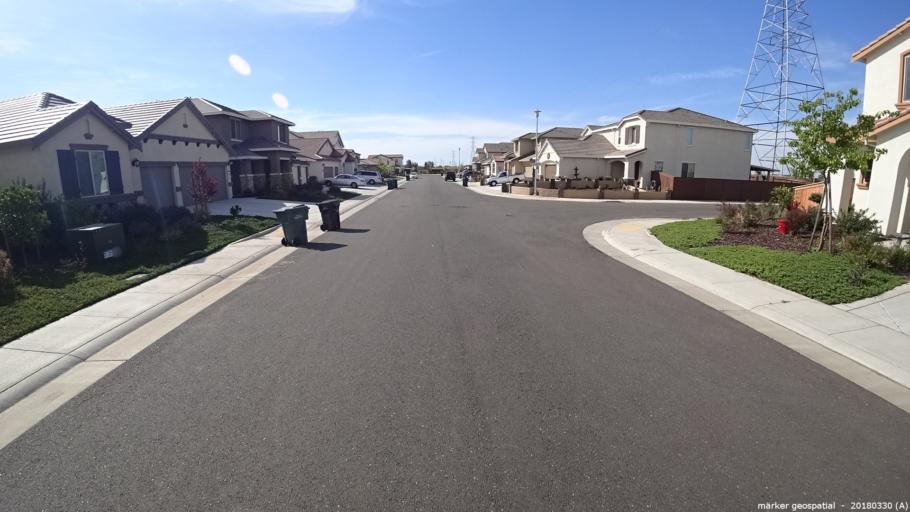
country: US
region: California
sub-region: Sacramento County
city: Vineyard
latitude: 38.4884
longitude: -121.3498
